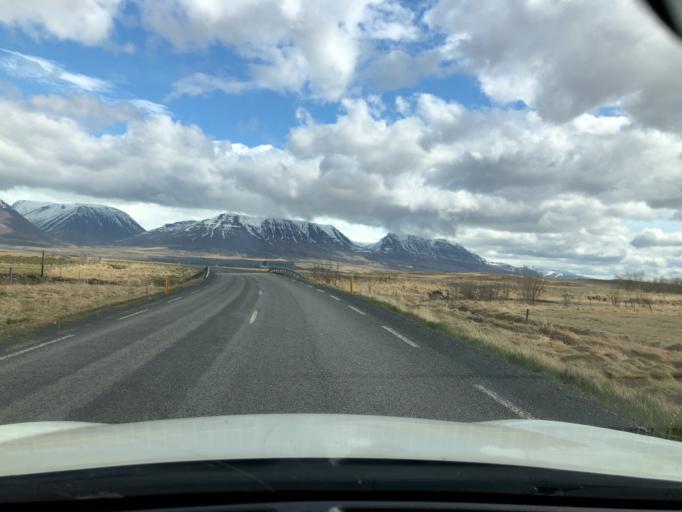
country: IS
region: Northwest
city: Saudarkrokur
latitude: 65.5443
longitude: -19.4694
